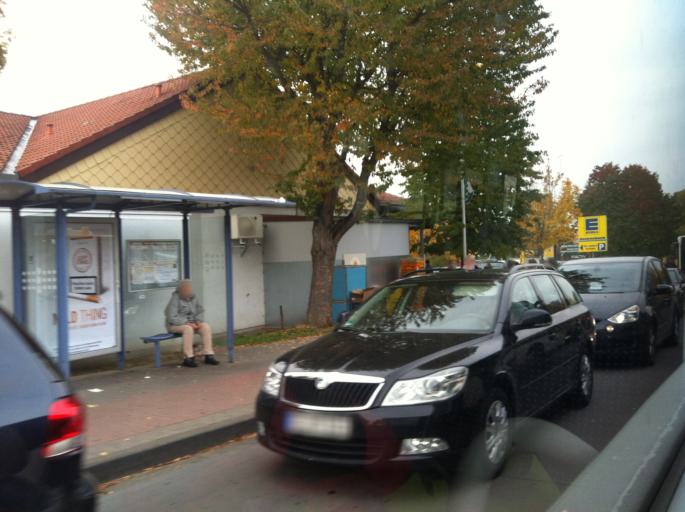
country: DE
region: Rheinland-Pfalz
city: Klein-Winternheim
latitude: 49.9694
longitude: 8.2368
